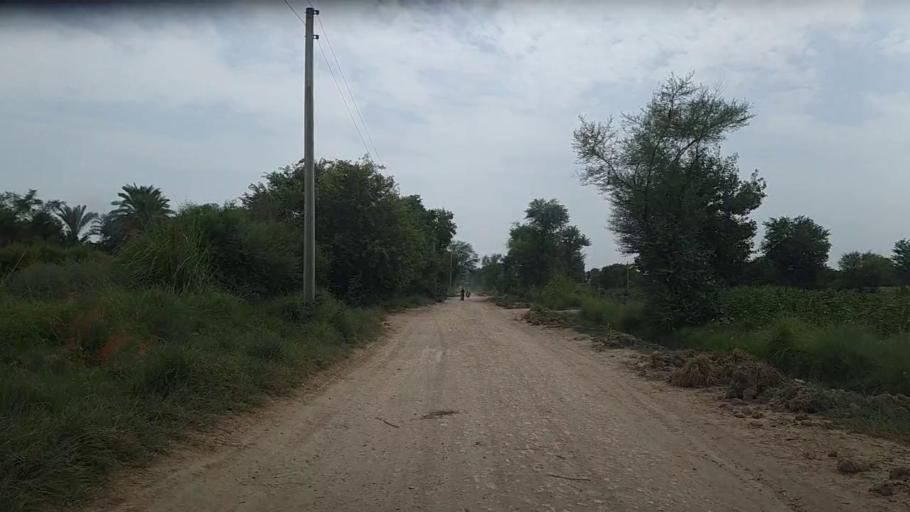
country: PK
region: Sindh
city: Bhiria
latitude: 26.8892
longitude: 68.2966
